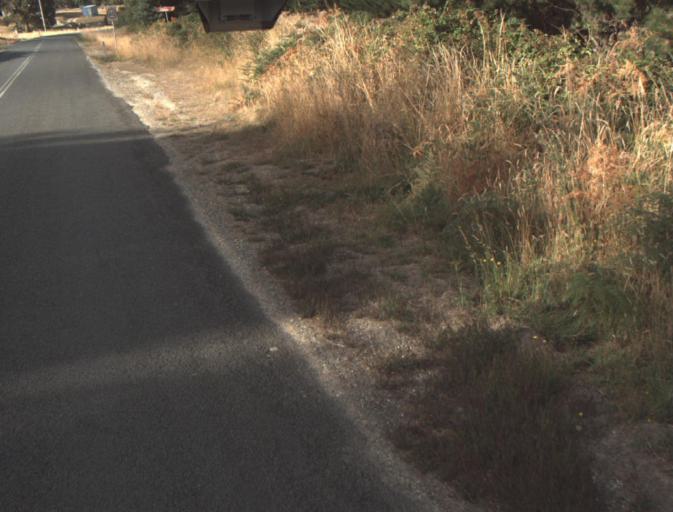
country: AU
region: Tasmania
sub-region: Launceston
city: Mayfield
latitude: -41.1733
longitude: 147.2301
